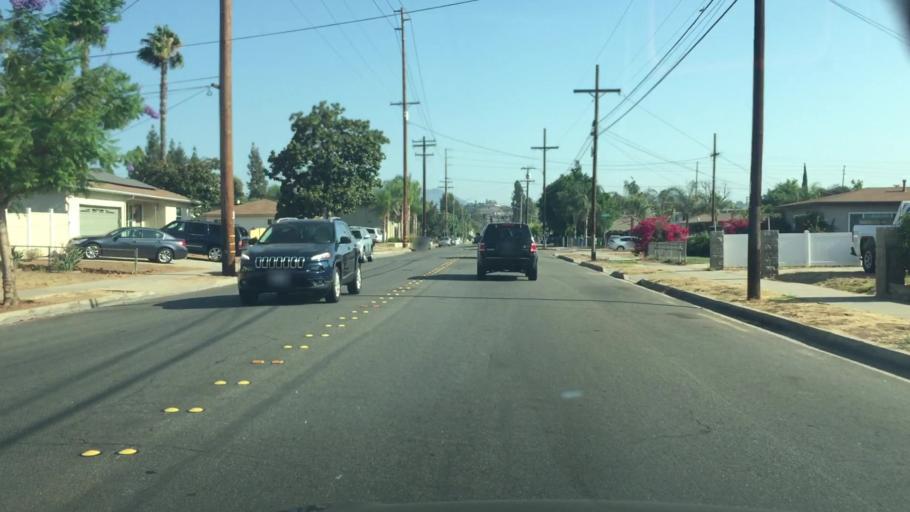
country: US
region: California
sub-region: San Diego County
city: Bostonia
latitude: 32.8023
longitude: -116.9446
